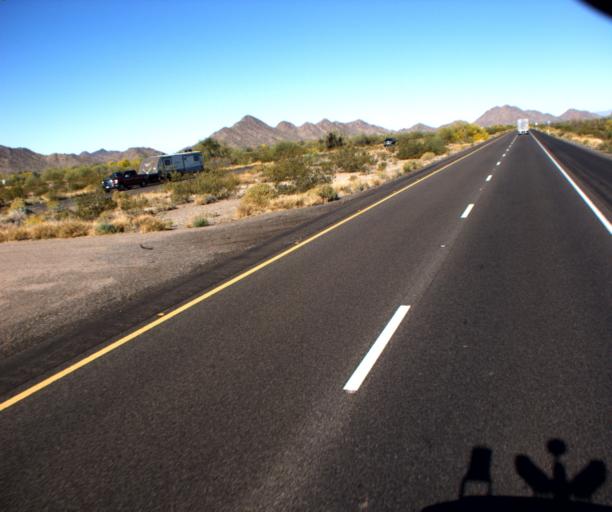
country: US
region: Arizona
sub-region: Maricopa County
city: Gila Bend
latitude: 32.8923
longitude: -112.4887
